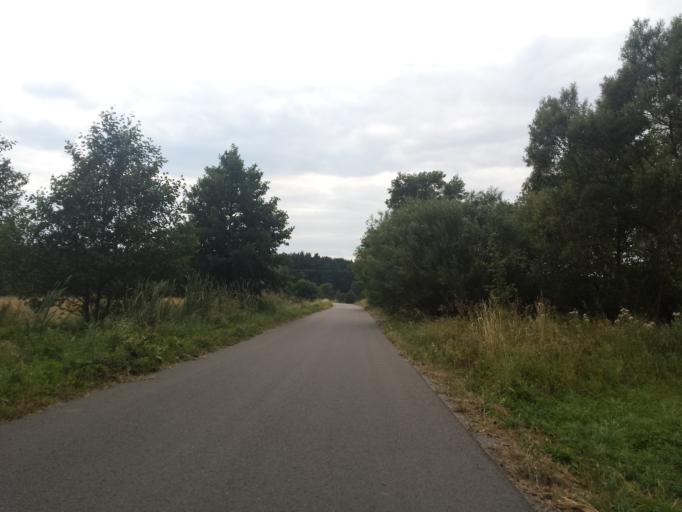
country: PL
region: Swietokrzyskie
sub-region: Powiat staszowski
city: Bogoria
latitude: 50.6578
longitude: 21.2273
